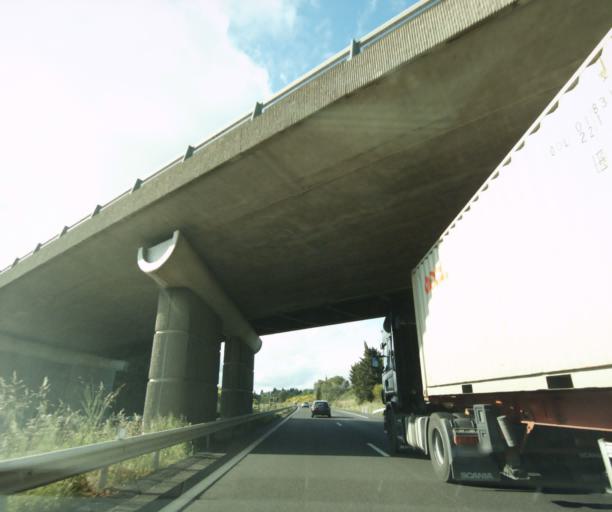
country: FR
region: Languedoc-Roussillon
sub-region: Departement du Gard
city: Garons
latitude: 43.7739
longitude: 4.4181
